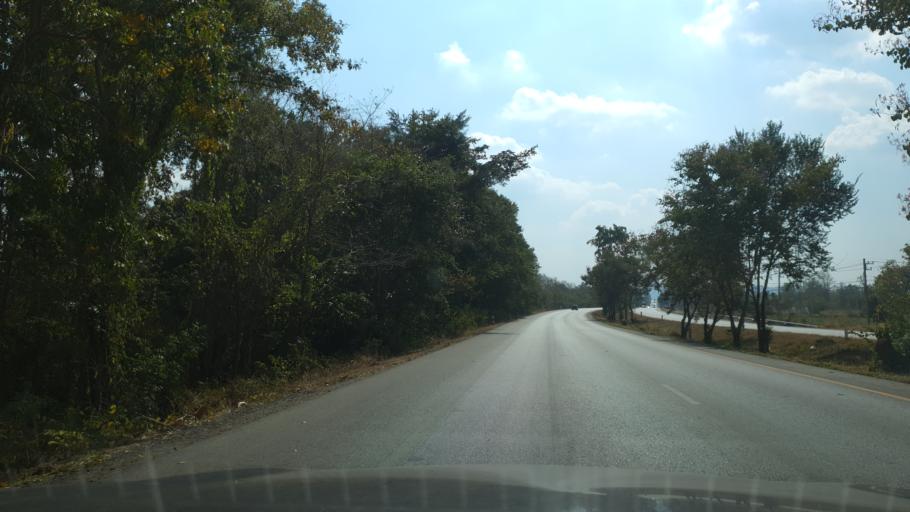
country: TH
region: Lampang
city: Mae Phrik
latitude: 17.4013
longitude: 99.1496
